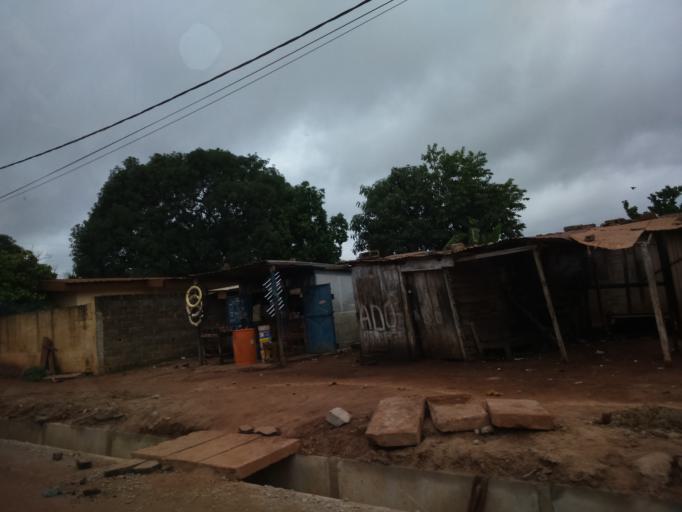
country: CI
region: Moyen-Comoe
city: Abengourou
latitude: 6.7261
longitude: -3.5028
